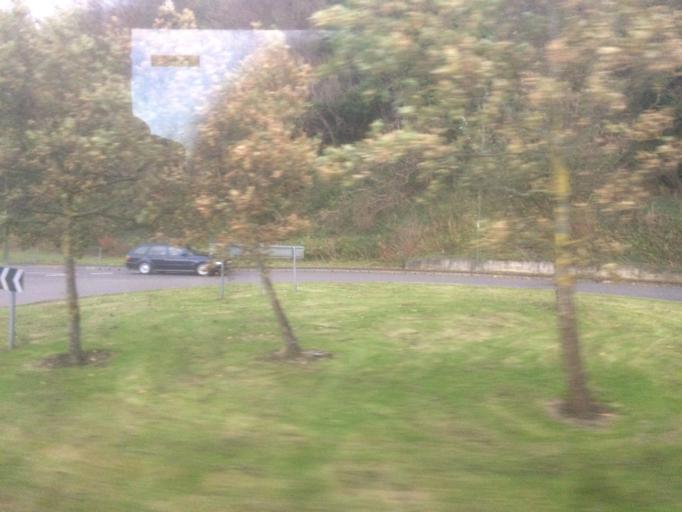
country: GB
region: Scotland
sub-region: Stirling
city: Stirling
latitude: 56.1266
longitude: -3.9494
